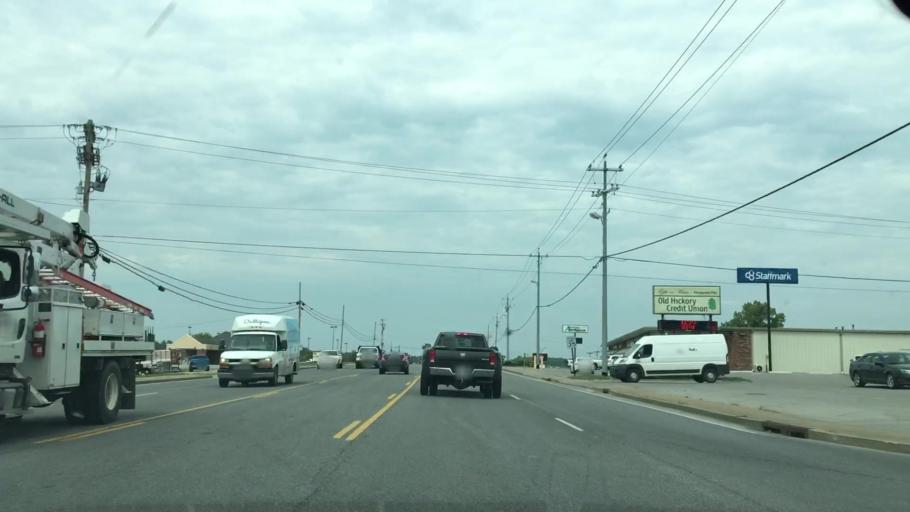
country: US
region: Tennessee
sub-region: Wilson County
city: Lebanon
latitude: 36.2151
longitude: -86.3270
